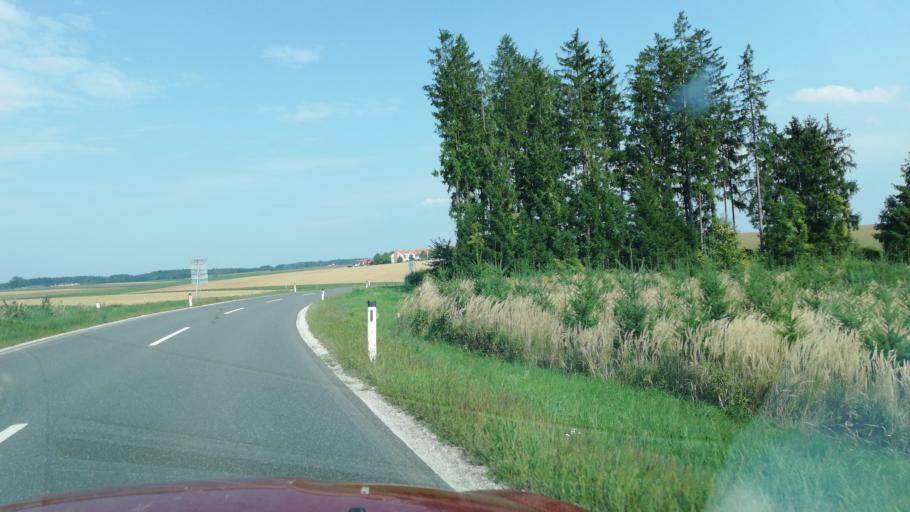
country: AT
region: Upper Austria
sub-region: Politischer Bezirk Steyr-Land
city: Sierning
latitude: 48.0438
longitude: 14.2914
